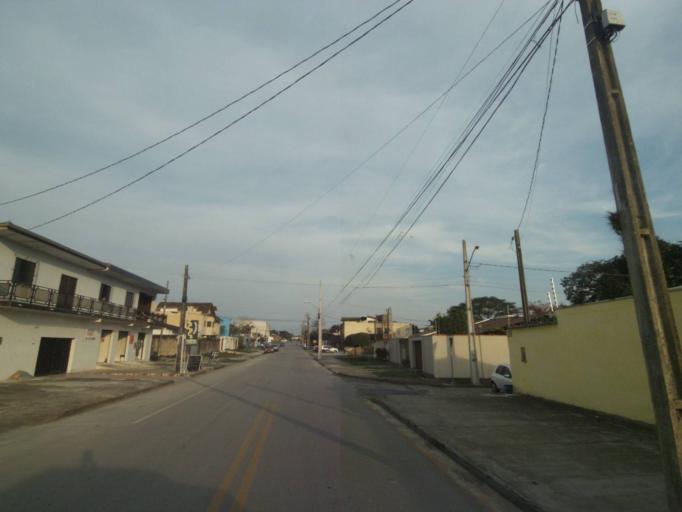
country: BR
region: Parana
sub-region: Paranagua
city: Paranagua
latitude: -25.5244
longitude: -48.5349
